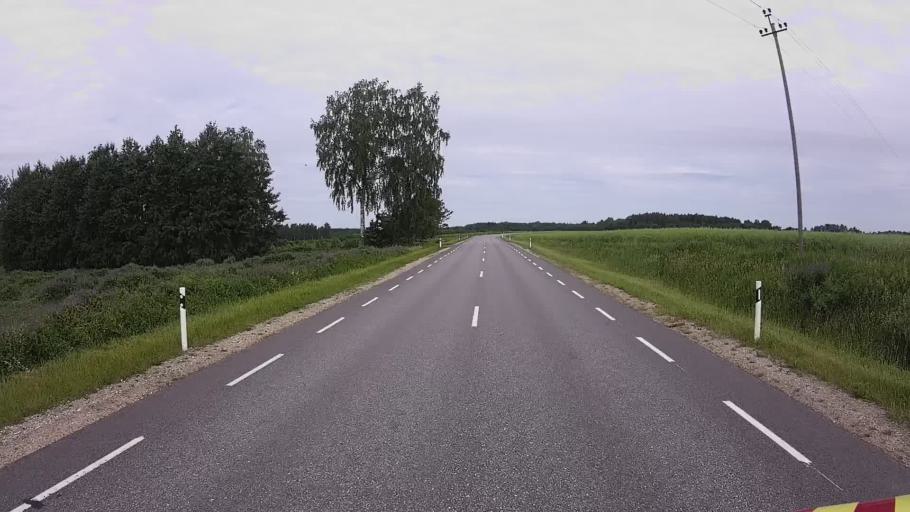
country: EE
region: Viljandimaa
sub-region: Karksi vald
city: Karksi-Nuia
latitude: 58.1658
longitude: 25.5818
